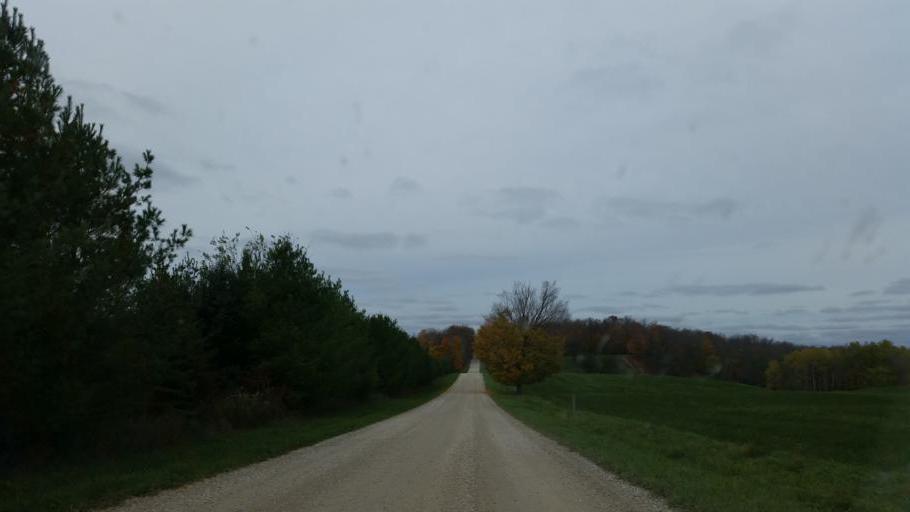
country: CA
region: Ontario
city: Wingham
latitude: 43.9799
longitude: -81.3335
